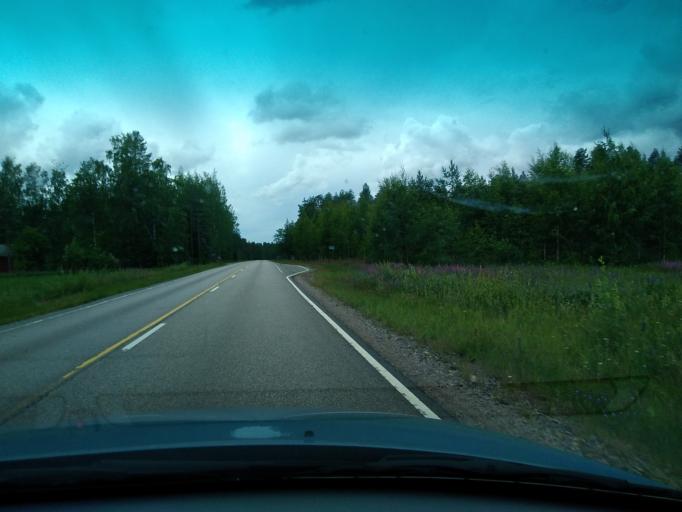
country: FI
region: Central Finland
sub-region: Saarijaervi-Viitasaari
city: Pylkoenmaeki
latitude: 62.6249
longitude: 24.7832
